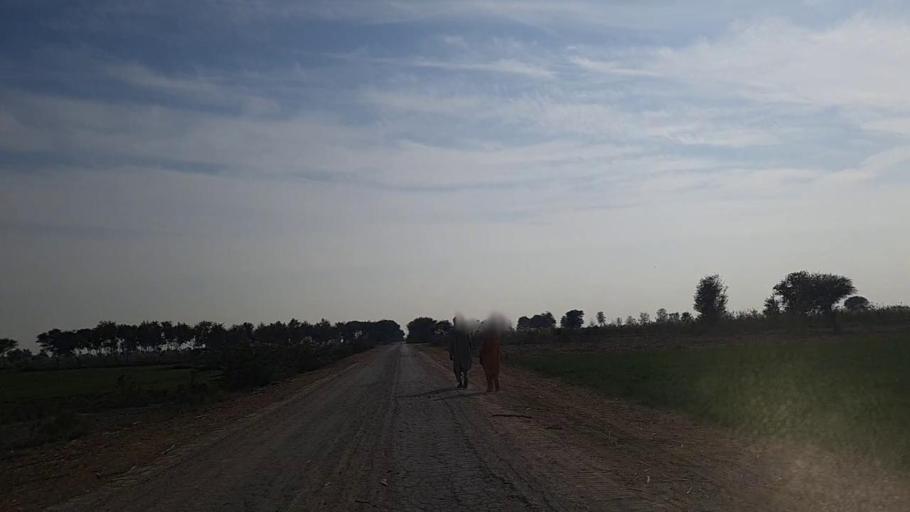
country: PK
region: Sindh
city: Daur
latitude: 26.4653
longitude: 68.4175
